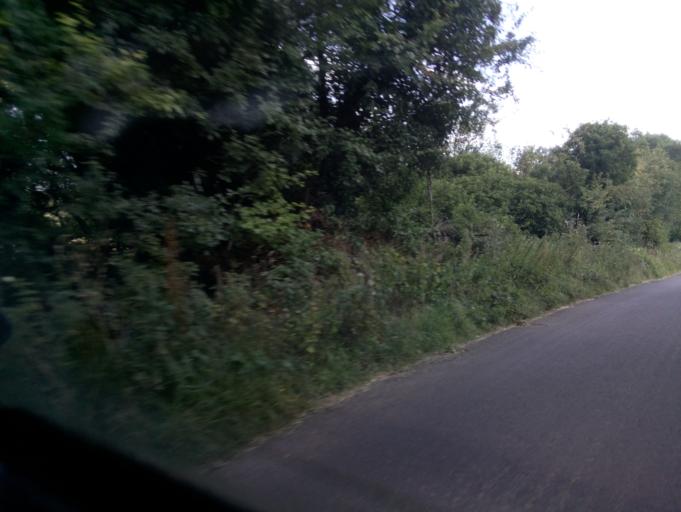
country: GB
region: England
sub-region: Gloucestershire
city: Tetbury
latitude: 51.6510
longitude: -2.1441
